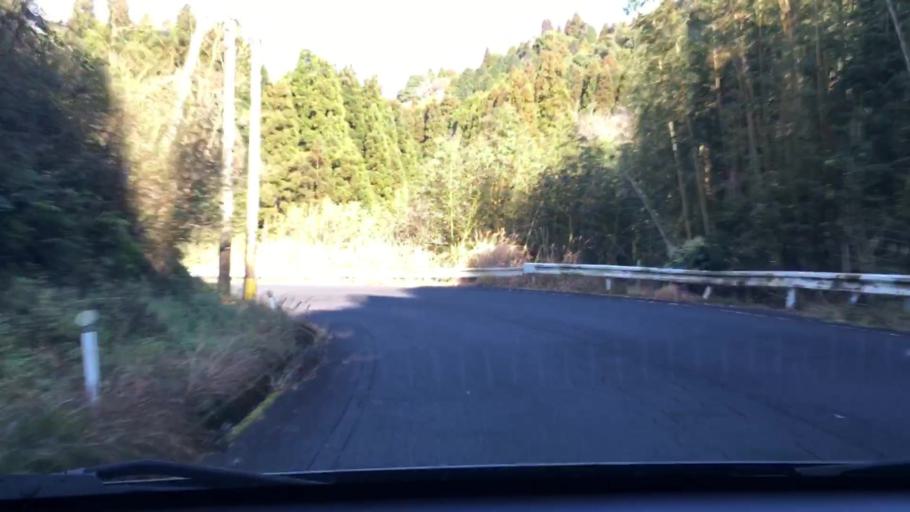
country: JP
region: Kagoshima
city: Kokubu-matsuki
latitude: 31.6684
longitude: 130.8306
